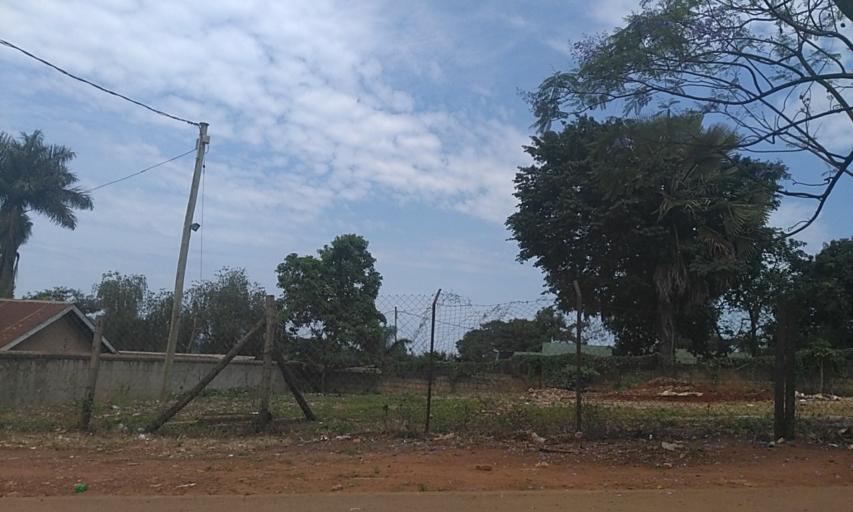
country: UG
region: Central Region
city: Kampala Central Division
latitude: 0.3058
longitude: 32.5496
